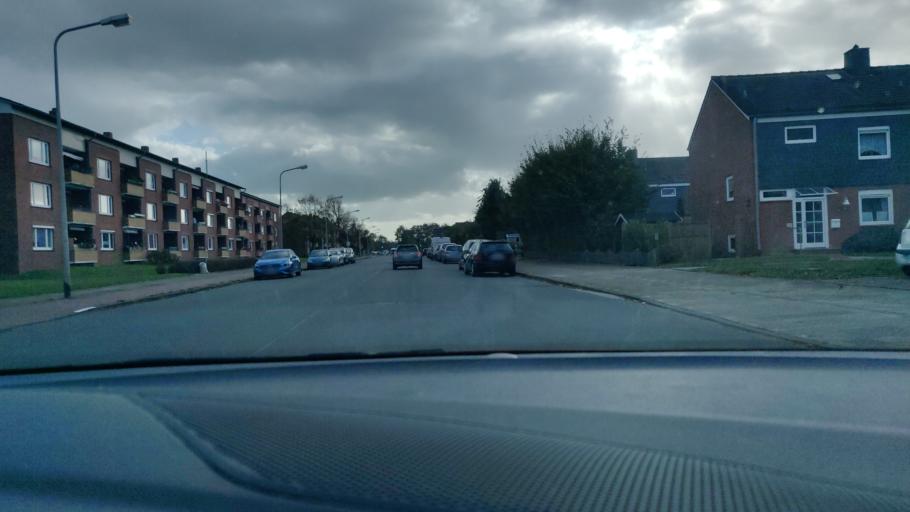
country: DE
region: Lower Saxony
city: Cuxhaven
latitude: 53.8704
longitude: 8.6781
